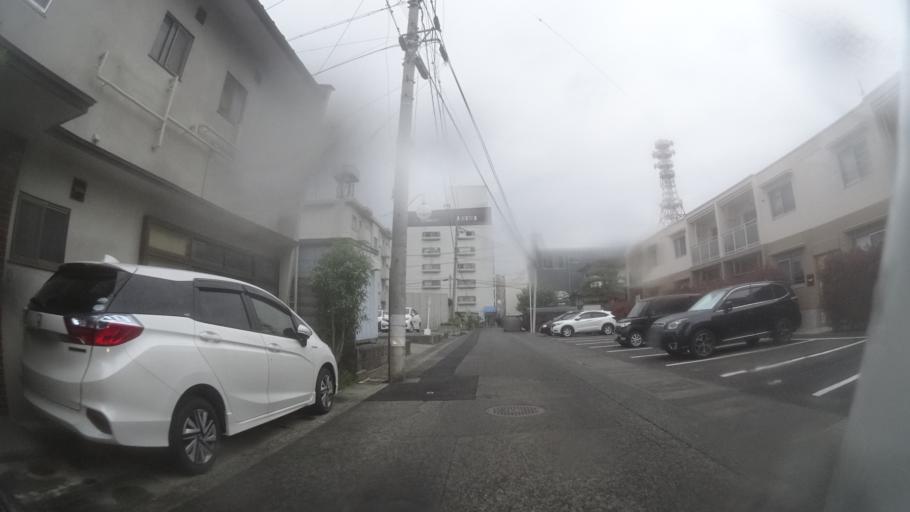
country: JP
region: Nagano
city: Nagano-shi
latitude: 36.6525
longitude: 138.1998
